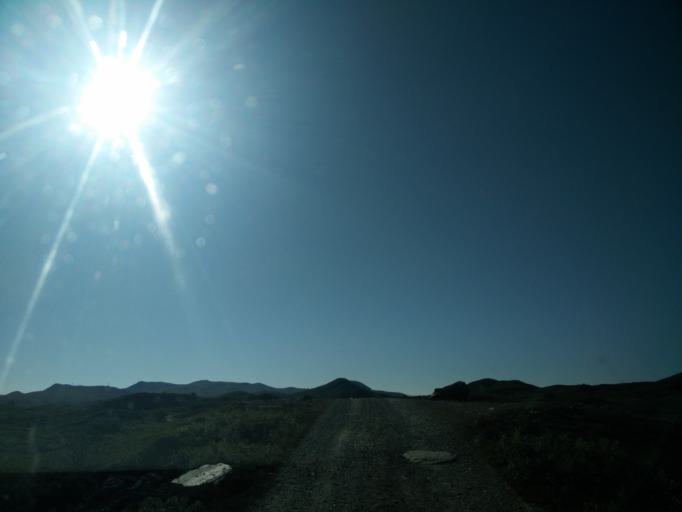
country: NO
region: Sor-Trondelag
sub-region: Tydal
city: Aas
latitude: 62.5682
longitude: 12.1984
